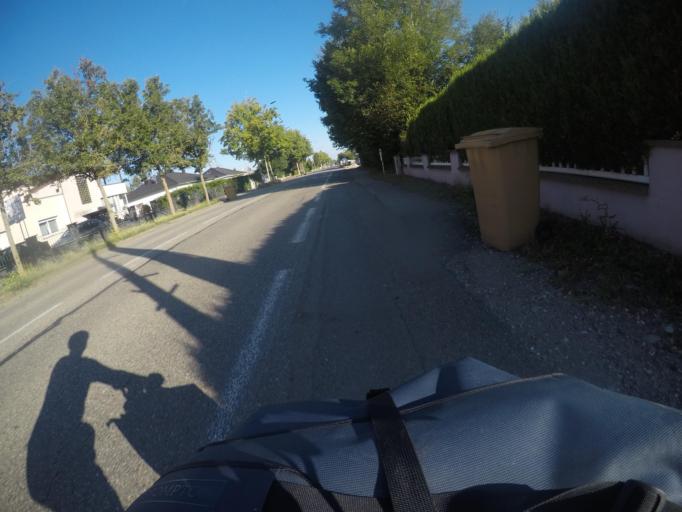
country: FR
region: Alsace
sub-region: Departement du Haut-Rhin
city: Rosenau
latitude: 47.6198
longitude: 7.5313
